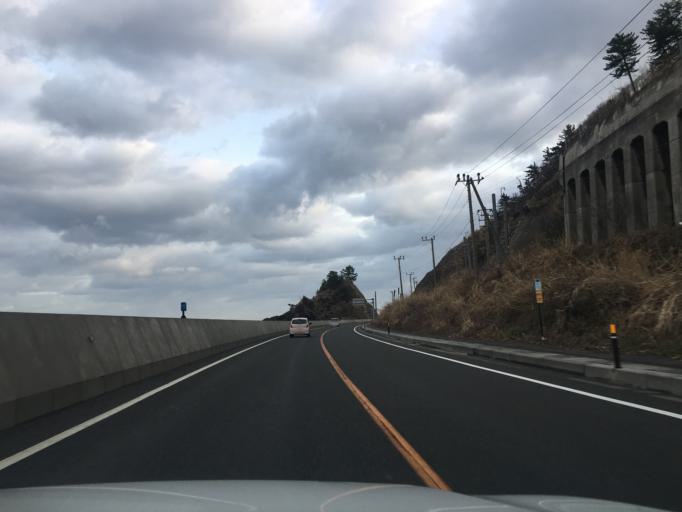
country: JP
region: Yamagata
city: Tsuruoka
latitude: 38.5837
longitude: 139.5600
